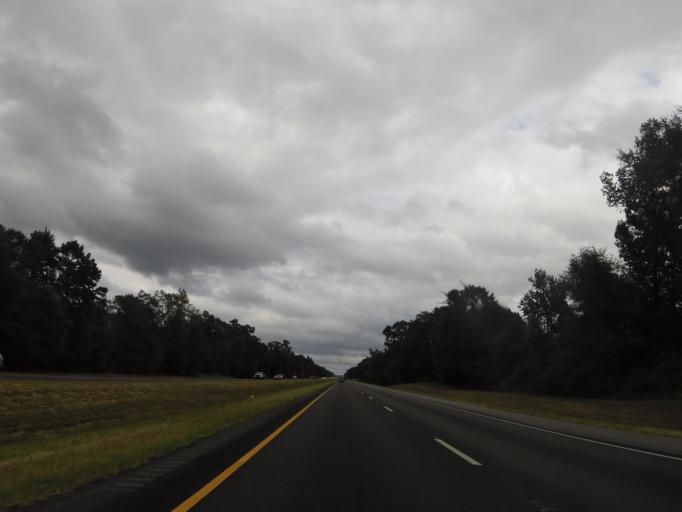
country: US
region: Alabama
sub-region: Conecuh County
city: Evergreen
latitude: 31.3939
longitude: -87.0280
